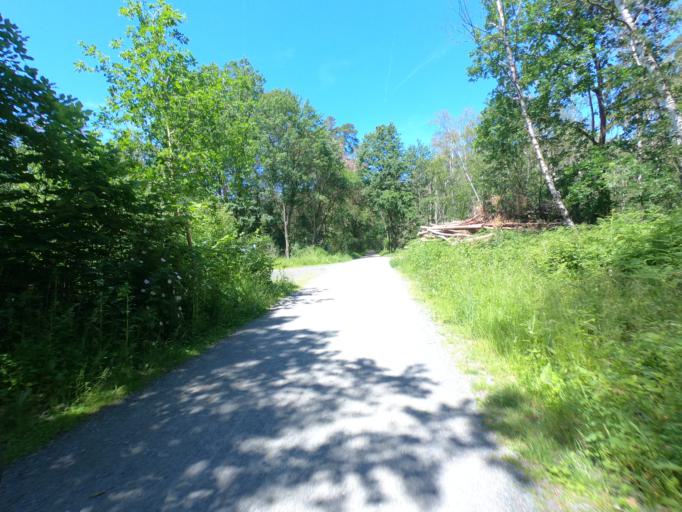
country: DE
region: Hesse
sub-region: Regierungsbezirk Darmstadt
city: Offenbach
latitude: 50.0622
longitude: 8.7513
